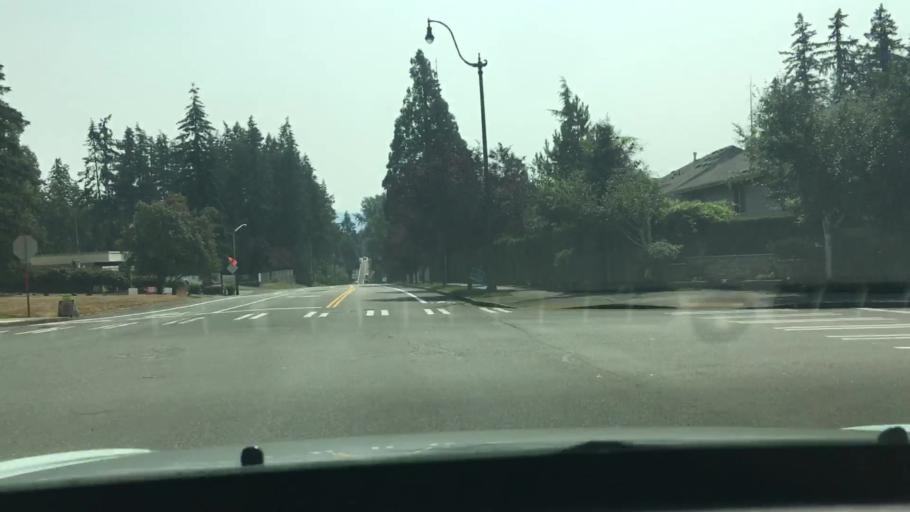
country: US
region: Washington
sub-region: King County
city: City of Sammamish
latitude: 47.5931
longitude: -122.0570
